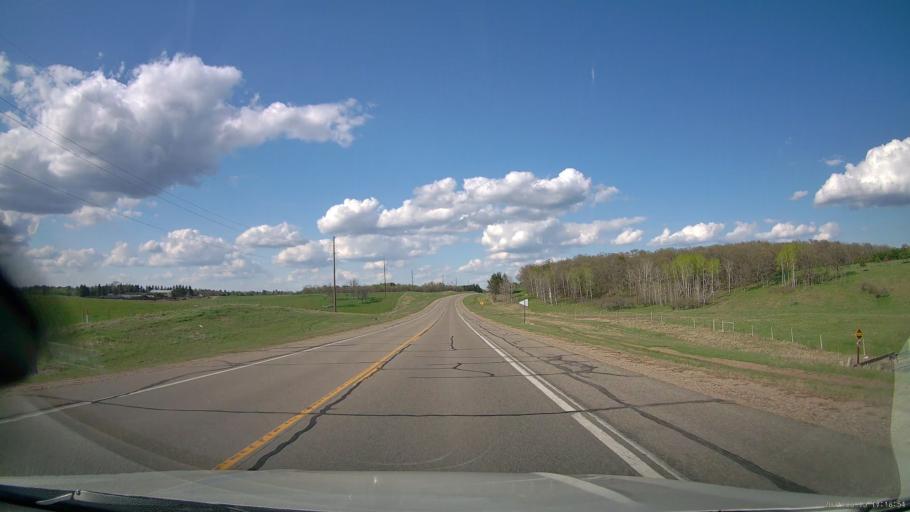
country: US
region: Minnesota
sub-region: Hubbard County
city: Park Rapids
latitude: 46.9689
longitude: -95.0153
